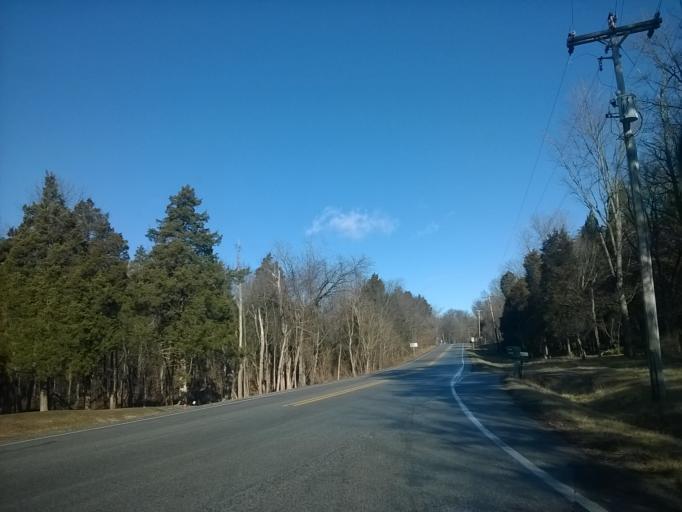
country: US
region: Indiana
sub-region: Scott County
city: Scottsburg
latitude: 38.7085
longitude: -85.6561
